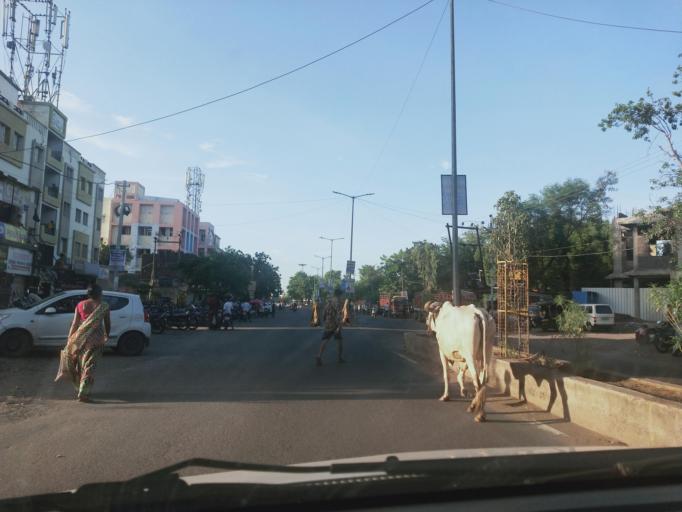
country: IN
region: Gujarat
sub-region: Bhavnagar
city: Bhavnagar
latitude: 21.7406
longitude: 72.1489
